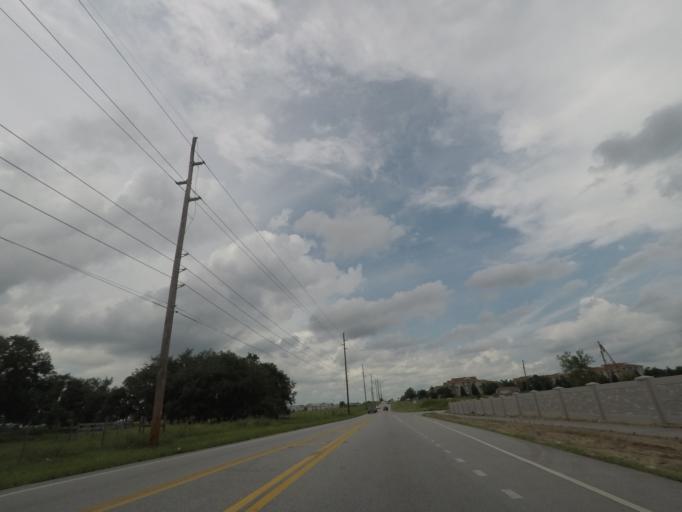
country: US
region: Florida
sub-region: Polk County
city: Loughman
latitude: 28.2514
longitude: -81.5905
